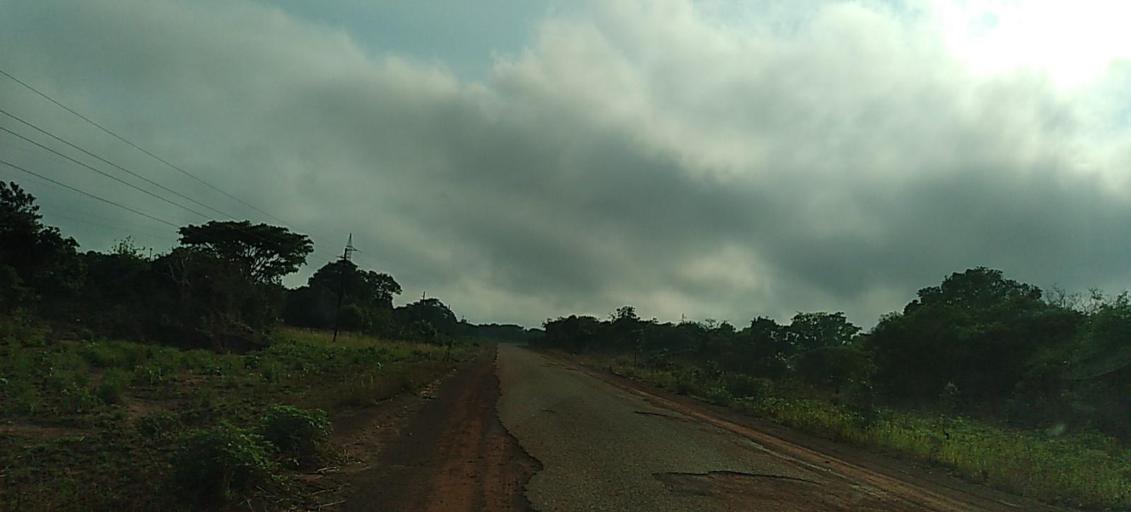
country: ZM
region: North-Western
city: Mwinilunga
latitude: -11.7268
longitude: 24.4932
